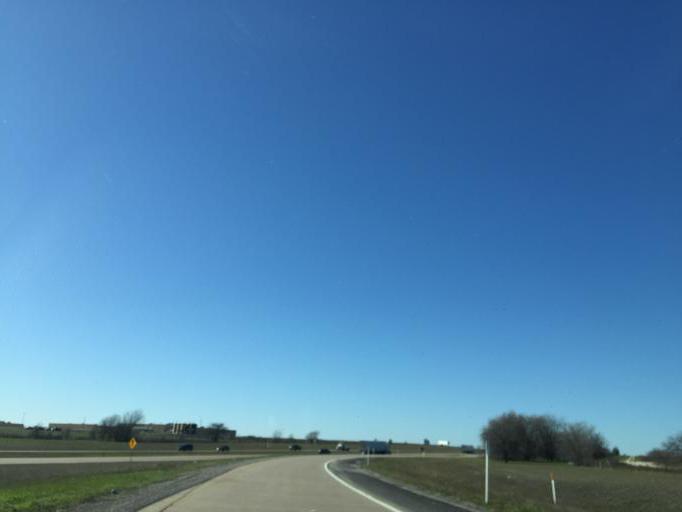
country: US
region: Texas
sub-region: Tarrant County
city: Benbrook
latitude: 32.6956
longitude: -97.5196
